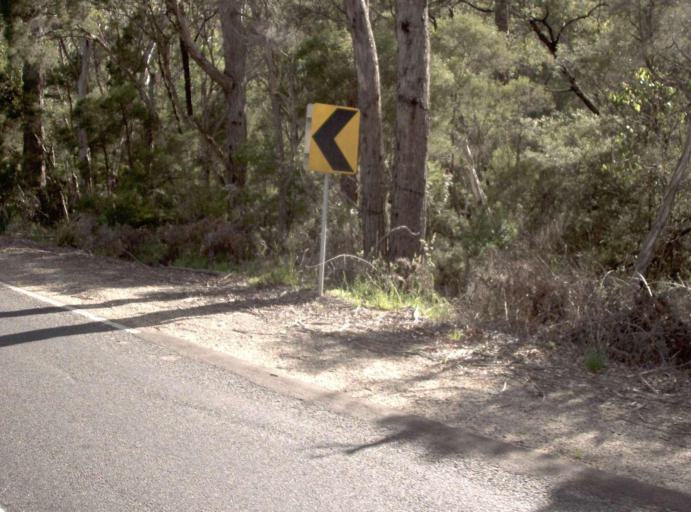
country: AU
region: Victoria
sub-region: East Gippsland
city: Lakes Entrance
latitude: -37.5491
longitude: 148.1484
